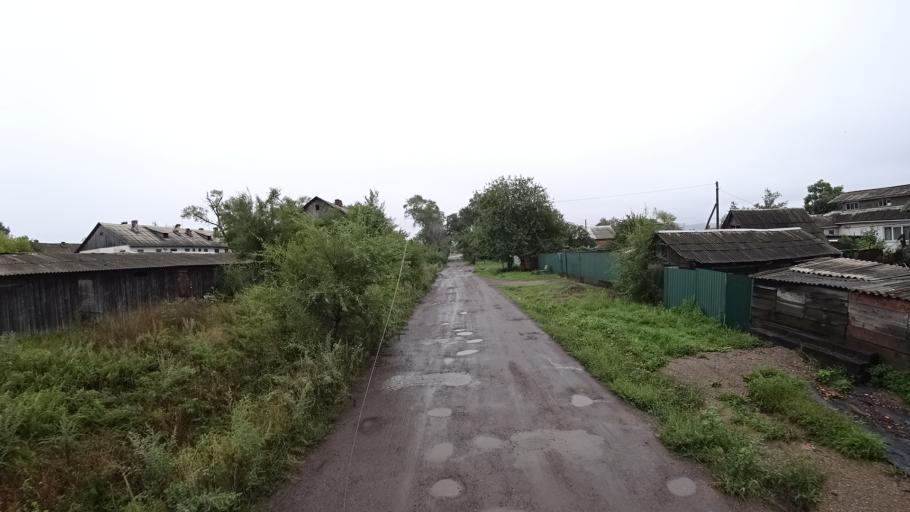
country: RU
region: Primorskiy
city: Monastyrishche
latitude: 44.1989
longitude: 132.4229
